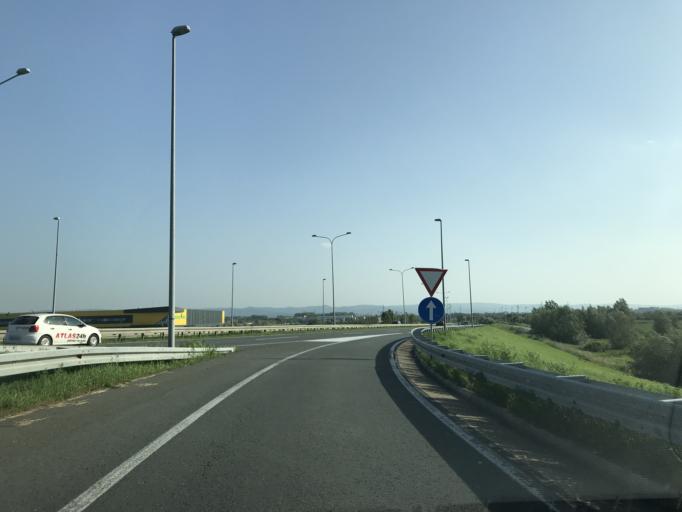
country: RS
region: Autonomna Pokrajina Vojvodina
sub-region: Juznobacki Okrug
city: Novi Sad
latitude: 45.3023
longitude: 19.8596
